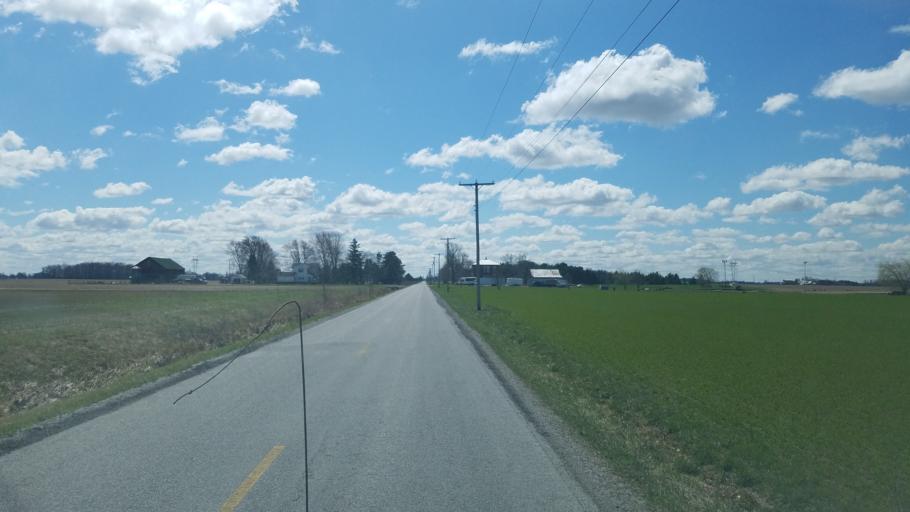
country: US
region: Ohio
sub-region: Seneca County
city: Fostoria
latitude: 41.1497
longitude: -83.4885
